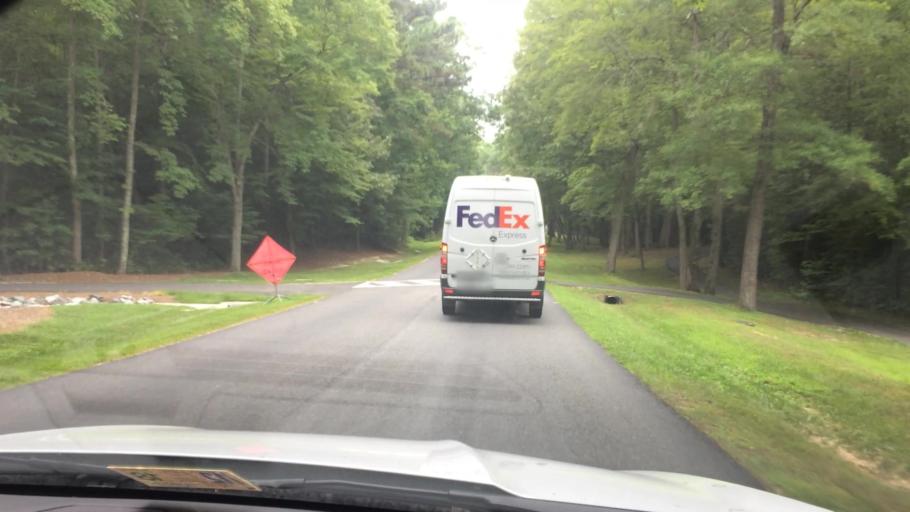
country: US
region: Virginia
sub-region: James City County
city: Williamsburg
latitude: 37.2932
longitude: -76.7922
